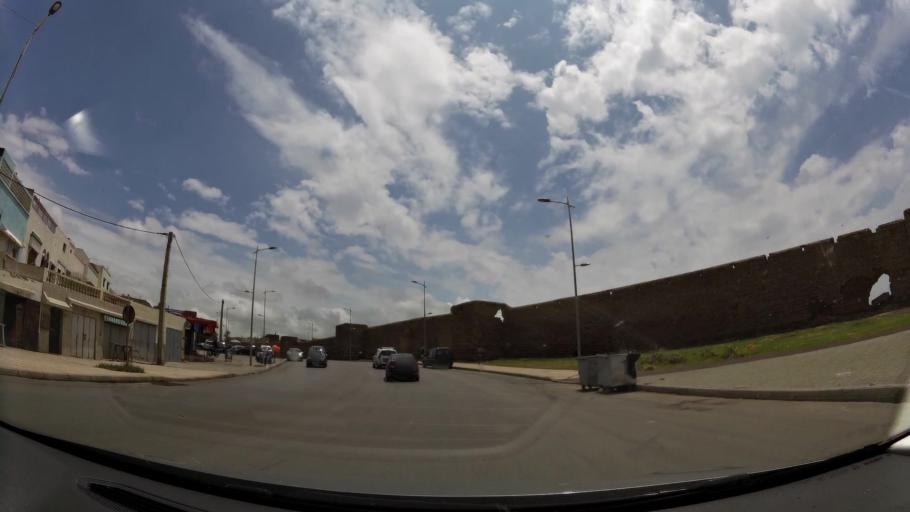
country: MA
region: Rabat-Sale-Zemmour-Zaer
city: Sale
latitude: 34.0465
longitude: -6.8281
